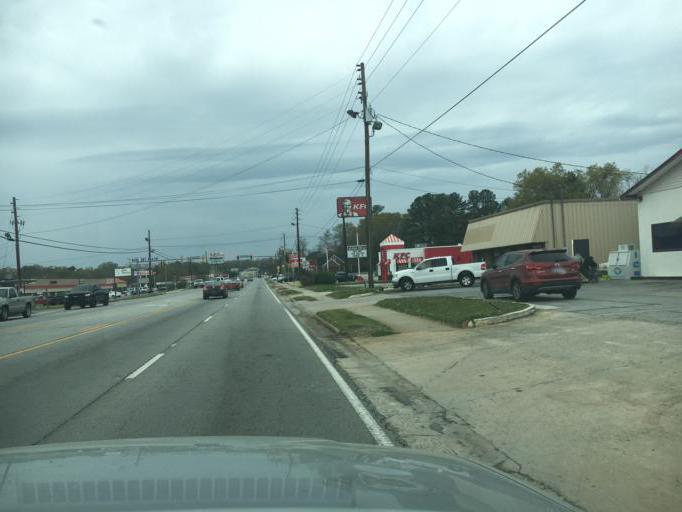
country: US
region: Georgia
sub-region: Stephens County
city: Toccoa
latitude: 34.5724
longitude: -83.3104
